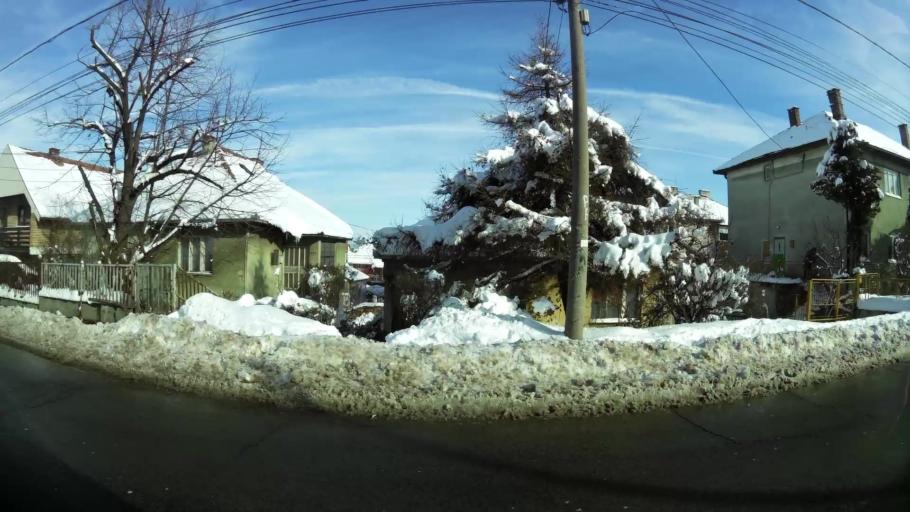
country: RS
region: Central Serbia
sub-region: Belgrade
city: Palilula
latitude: 44.8056
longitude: 20.5173
